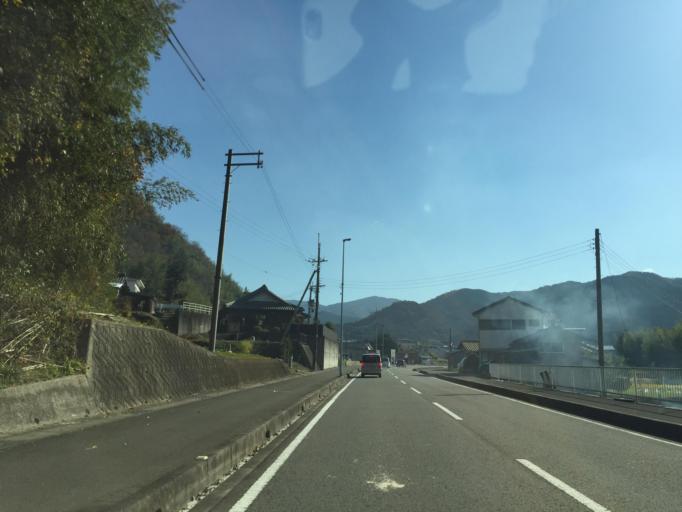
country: JP
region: Wakayama
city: Iwade
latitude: 34.1609
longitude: 135.3096
